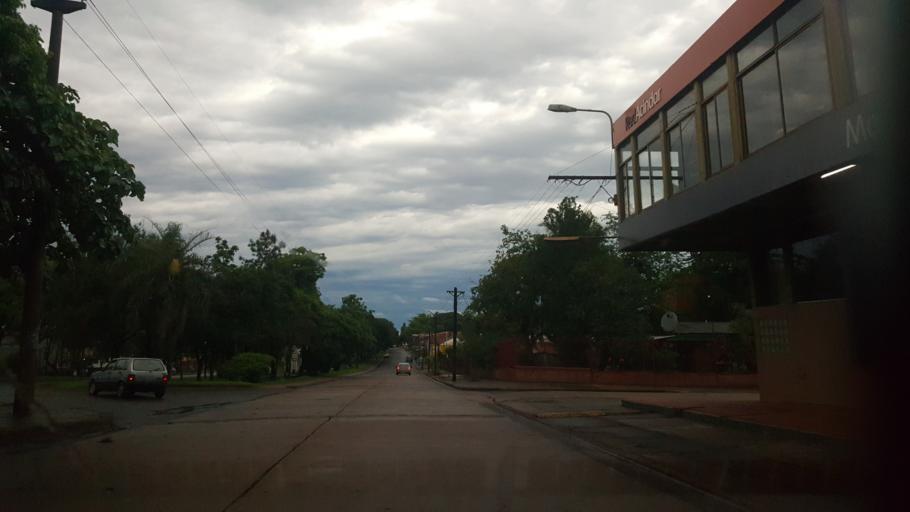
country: AR
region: Misiones
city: Jardin America
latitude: -27.0457
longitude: -55.2392
